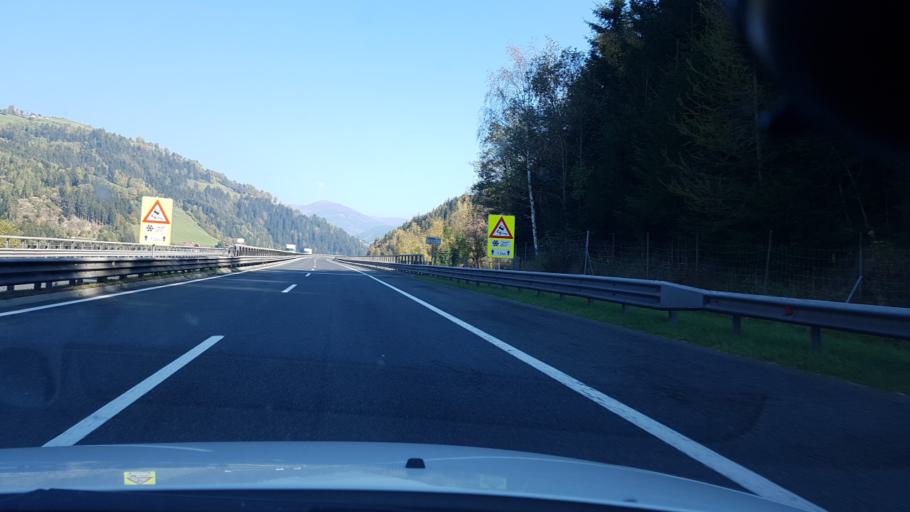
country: AT
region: Carinthia
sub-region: Politischer Bezirk Spittal an der Drau
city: Gmuend
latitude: 46.9126
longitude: 13.5578
